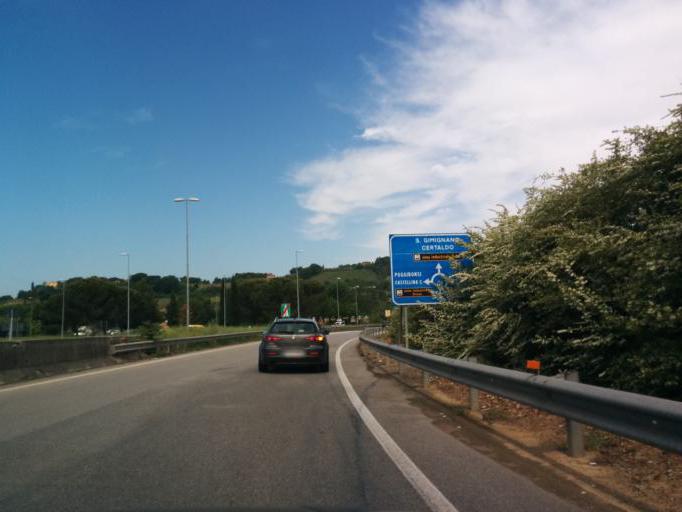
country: IT
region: Tuscany
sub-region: Provincia di Siena
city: Poggibonsi
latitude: 43.4861
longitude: 11.1521
